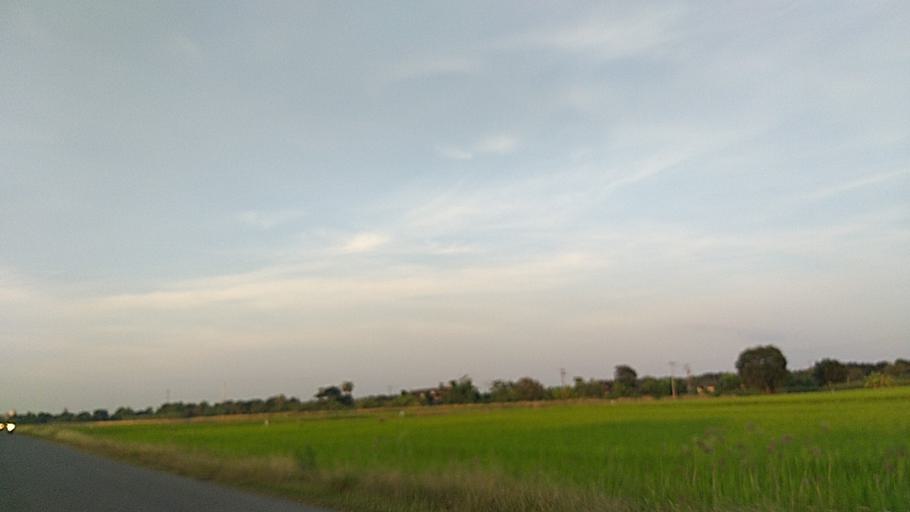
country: TH
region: Pathum Thani
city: Nong Suea
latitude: 14.0581
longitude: 100.8675
